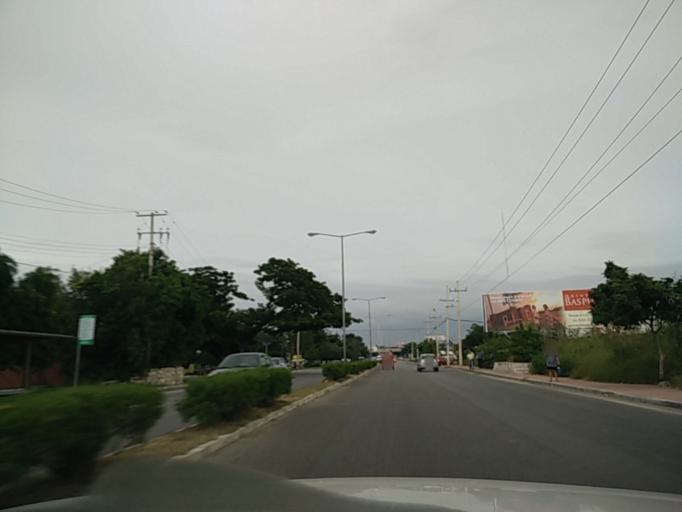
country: MX
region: Yucatan
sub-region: Kanasin
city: Kanasin
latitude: 20.9575
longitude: -89.5719
